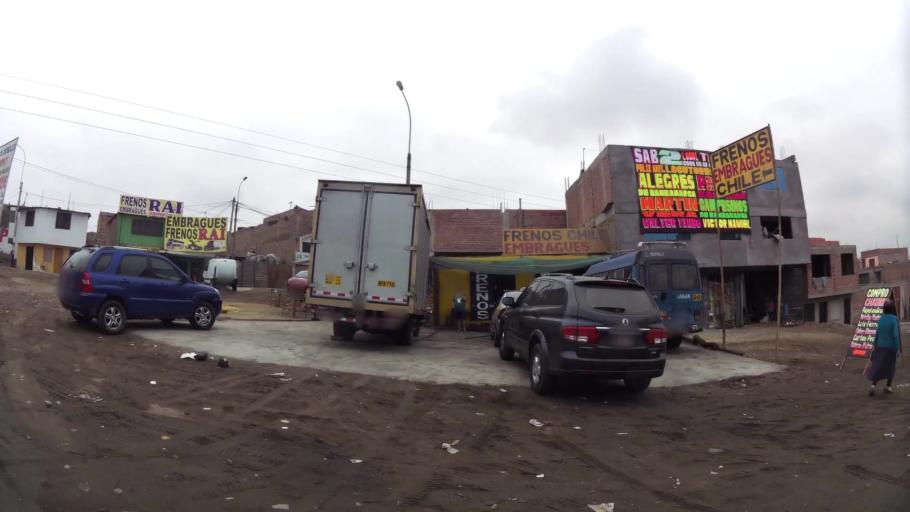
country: PE
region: Lima
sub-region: Lima
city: Surco
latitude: -12.1895
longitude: -76.9864
